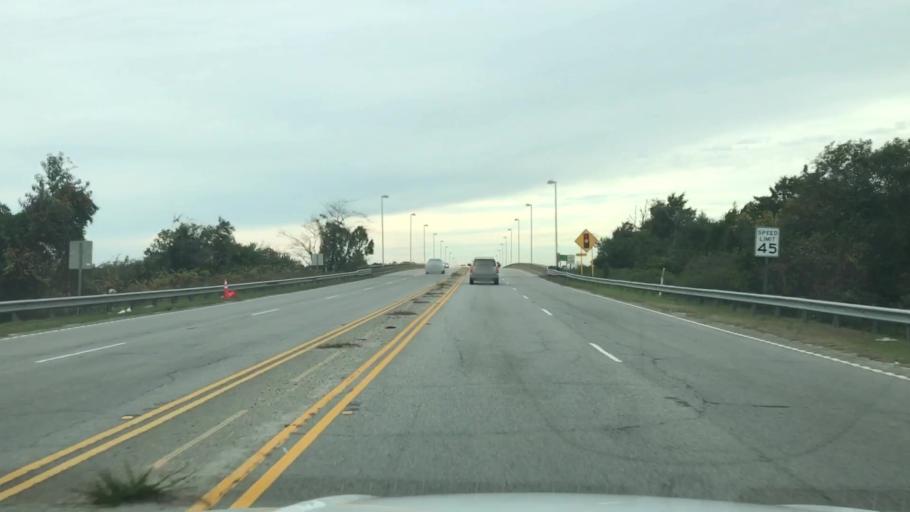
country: US
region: South Carolina
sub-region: Georgetown County
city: Georgetown
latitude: 33.3666
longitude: -79.2625
